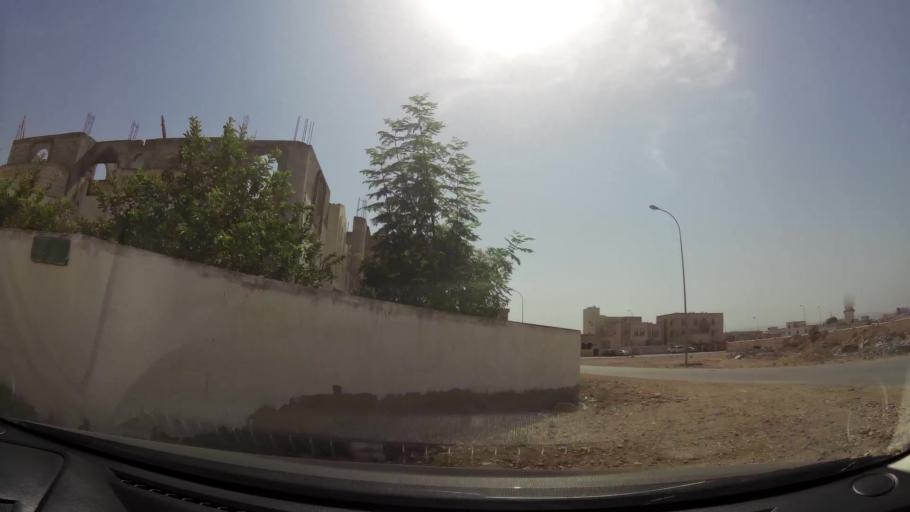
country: OM
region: Zufar
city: Salalah
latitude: 17.0463
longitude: 54.1521
